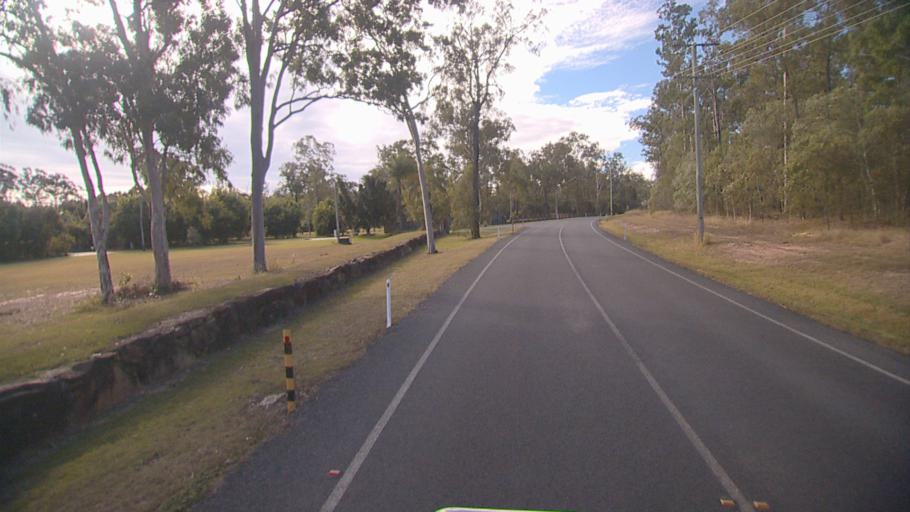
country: AU
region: Queensland
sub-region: Logan
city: North Maclean
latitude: -27.8126
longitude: 153.0566
